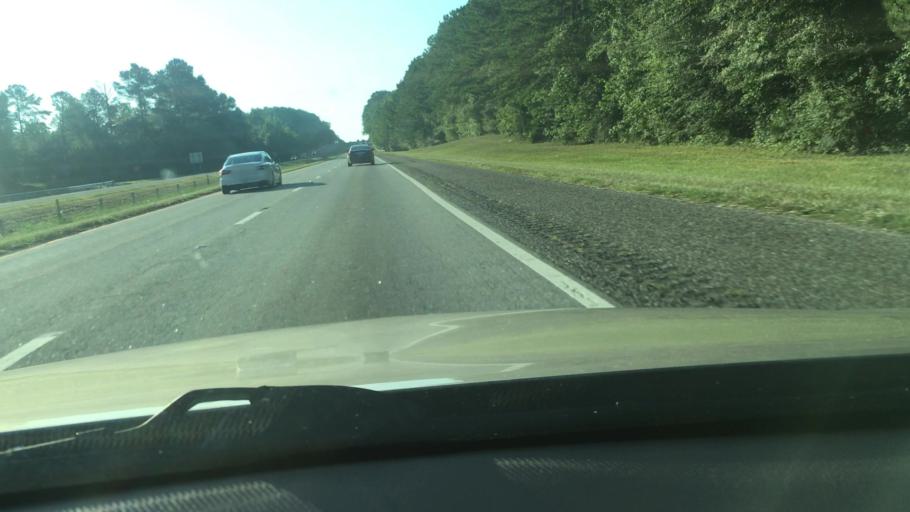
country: US
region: South Carolina
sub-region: Richland County
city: Lake Murray of Richland
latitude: 34.1636
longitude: -81.2840
